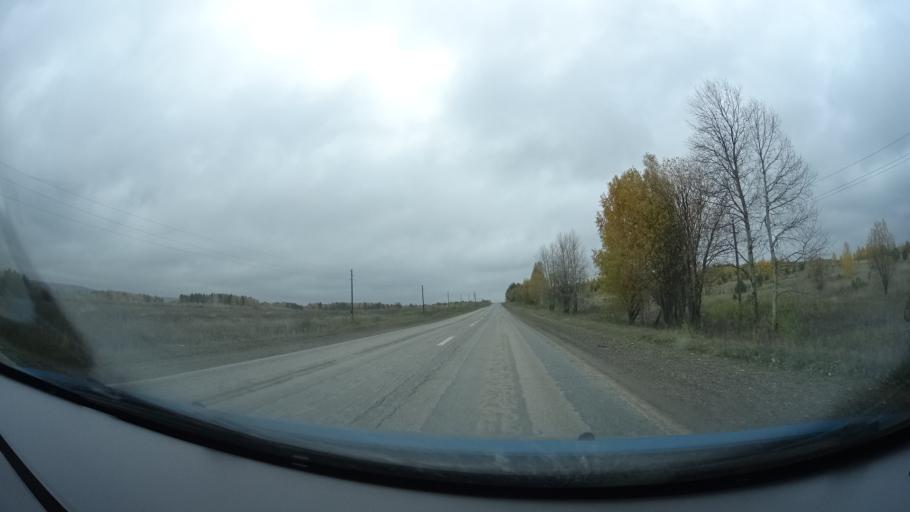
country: RU
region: Perm
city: Osa
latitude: 57.1329
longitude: 55.5262
